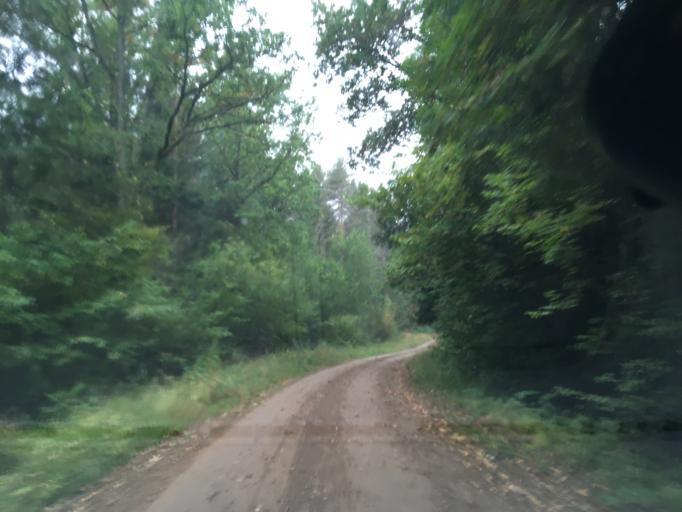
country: LV
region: Kuldigas Rajons
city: Kuldiga
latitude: 56.9870
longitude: 22.0072
